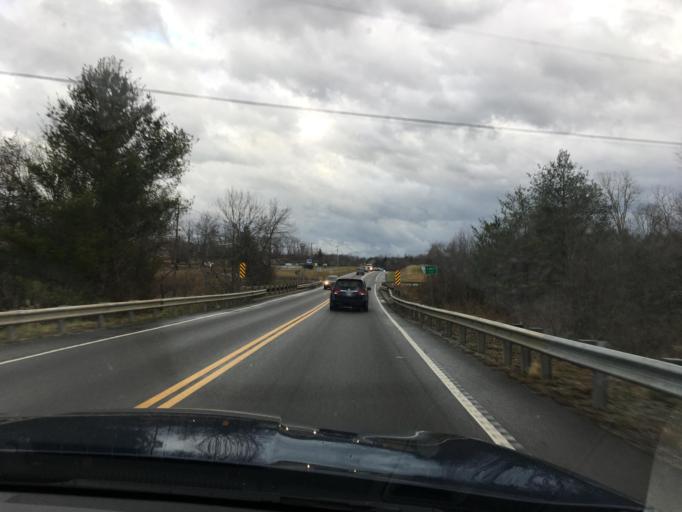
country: US
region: Tennessee
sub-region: Cumberland County
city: Crossville
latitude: 35.9173
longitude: -84.9960
